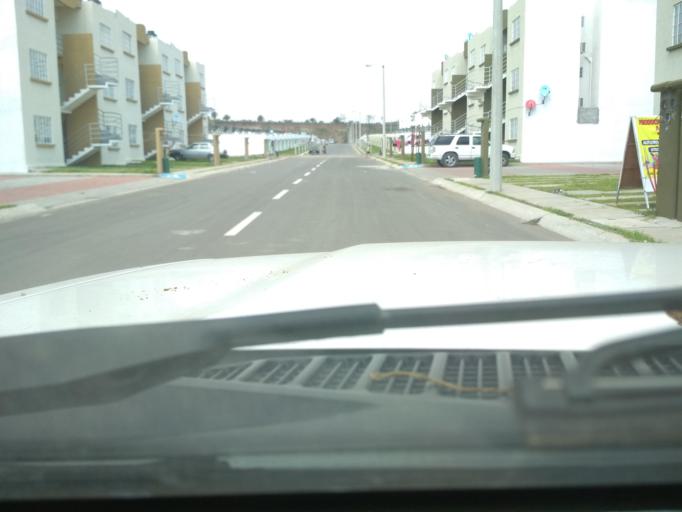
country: MX
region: Veracruz
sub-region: Veracruz
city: Lomas de Rio Medio Cuatro
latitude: 19.1845
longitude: -96.2124
